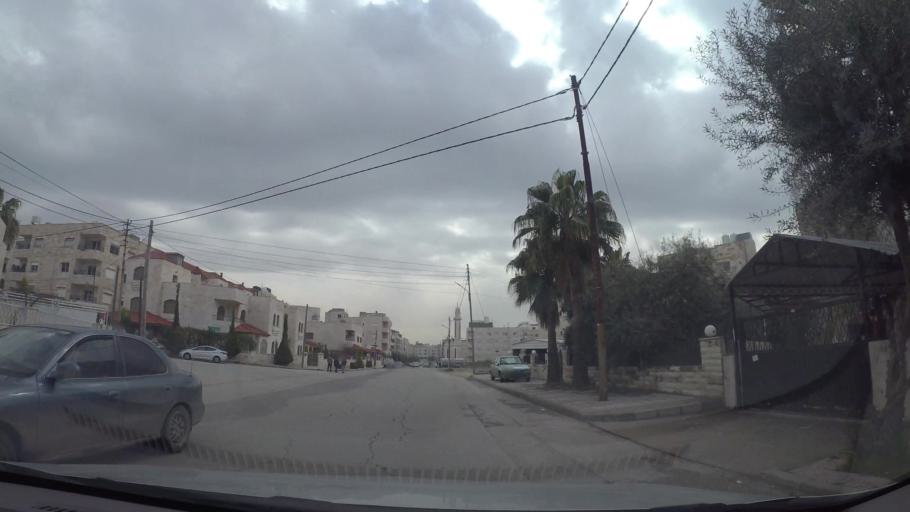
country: JO
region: Amman
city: Umm as Summaq
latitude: 31.8947
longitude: 35.8413
